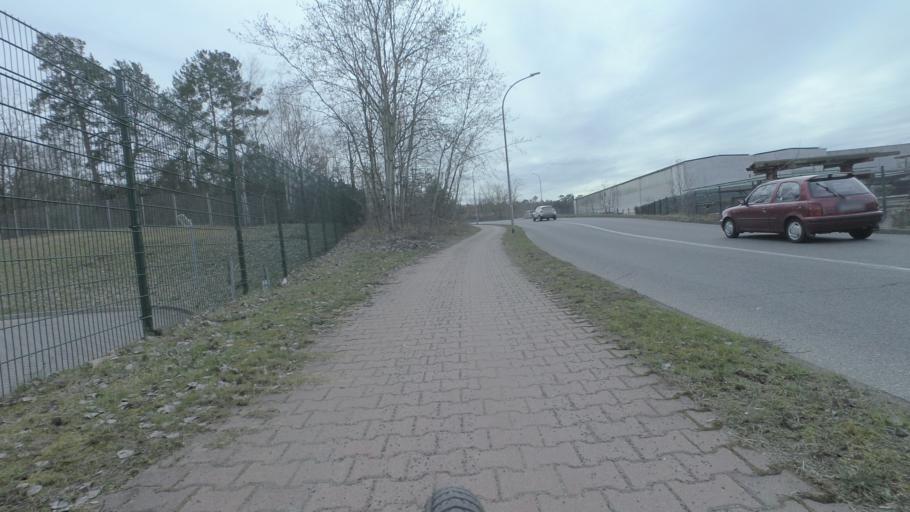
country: DE
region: Brandenburg
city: Ludwigsfelde
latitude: 52.3219
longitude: 13.2635
